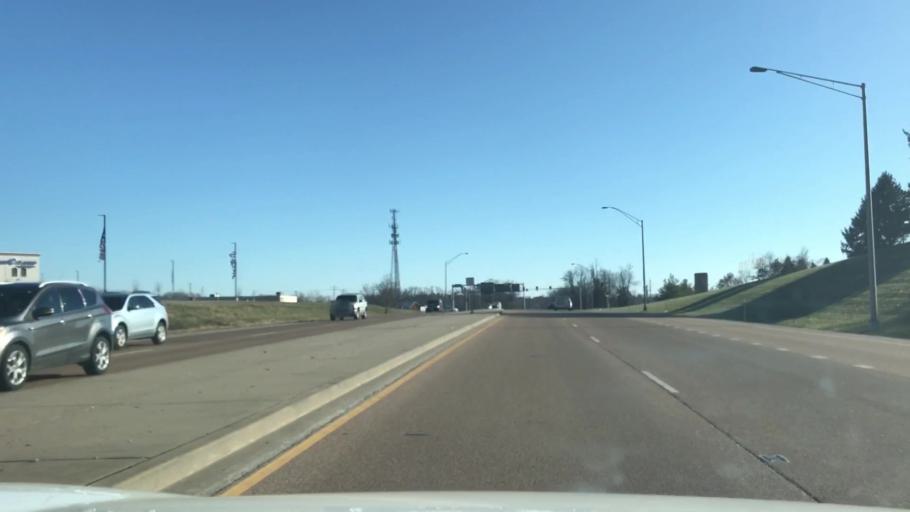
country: US
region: Illinois
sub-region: Saint Clair County
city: Alorton
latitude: 38.5631
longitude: -90.0865
